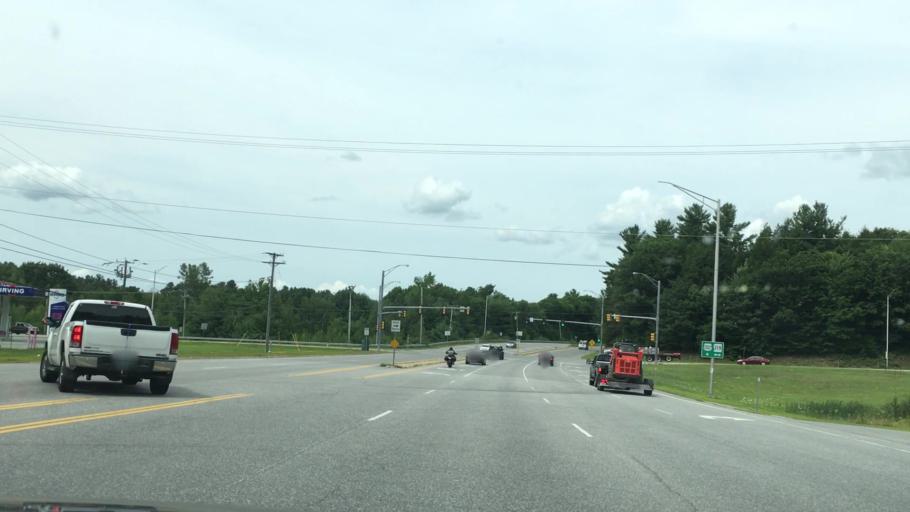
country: US
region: New Hampshire
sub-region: Cheshire County
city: Rindge
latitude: 42.7611
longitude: -72.0385
